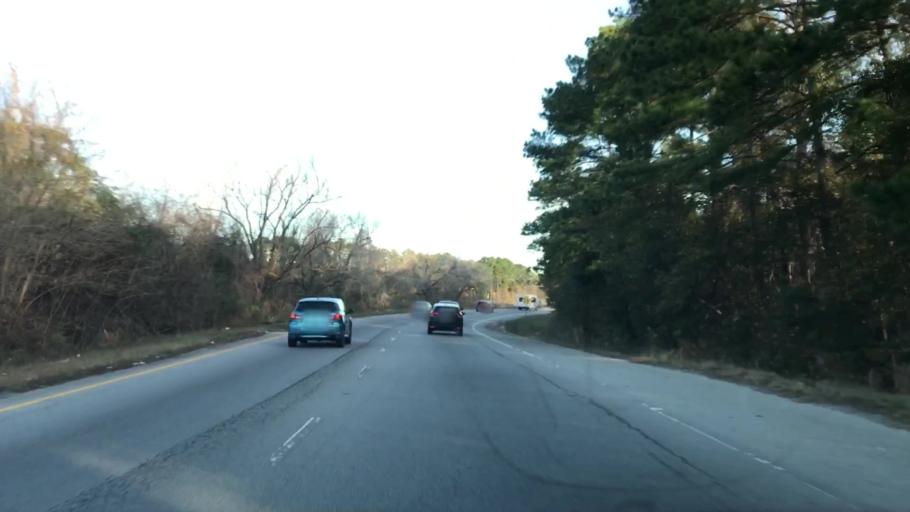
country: US
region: South Carolina
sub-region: Charleston County
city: North Charleston
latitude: 32.8101
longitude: -80.0349
